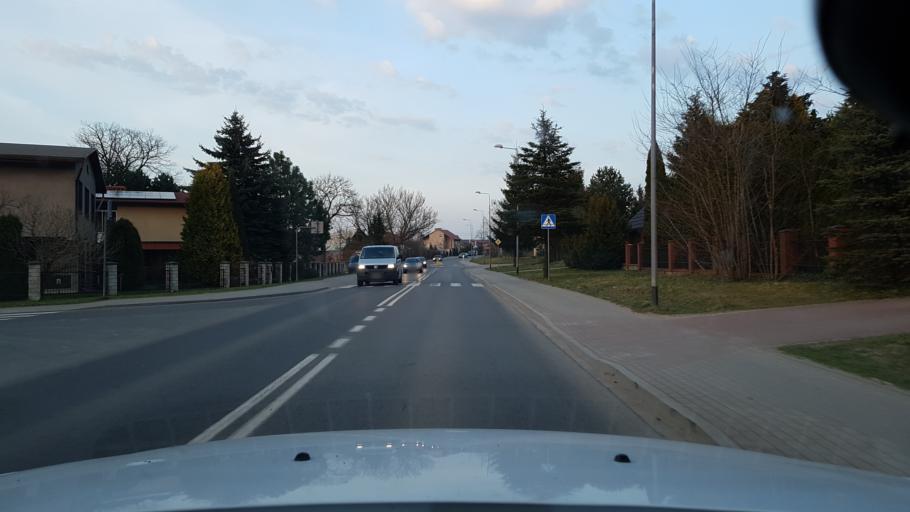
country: PL
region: West Pomeranian Voivodeship
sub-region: Koszalin
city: Koszalin
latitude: 54.1540
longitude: 16.2056
